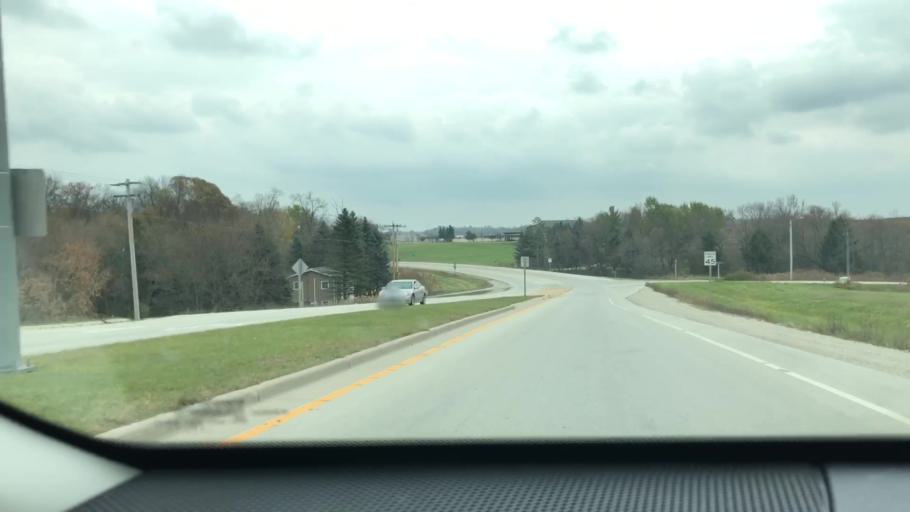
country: US
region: Wisconsin
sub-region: Brown County
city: Oneida
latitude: 44.4994
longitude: -88.1757
